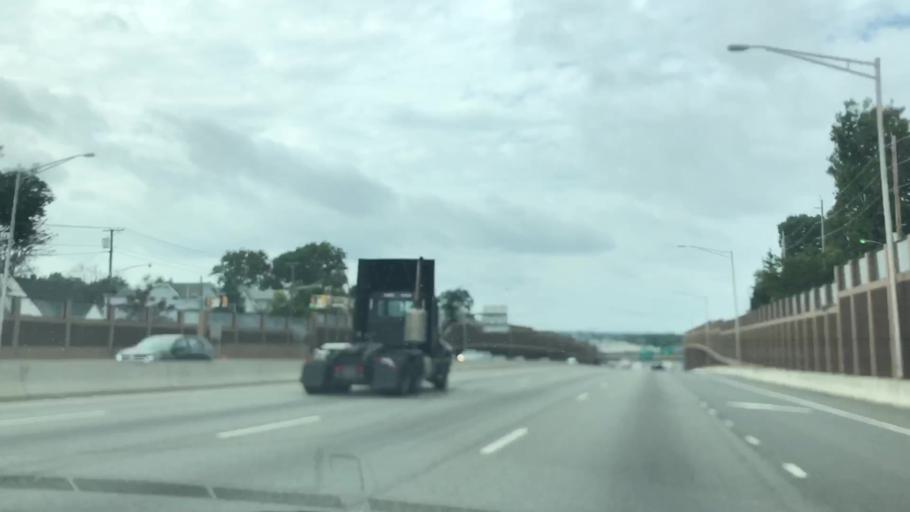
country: US
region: New Jersey
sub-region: Bergen County
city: Lyndhurst
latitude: 40.8186
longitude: -74.1166
